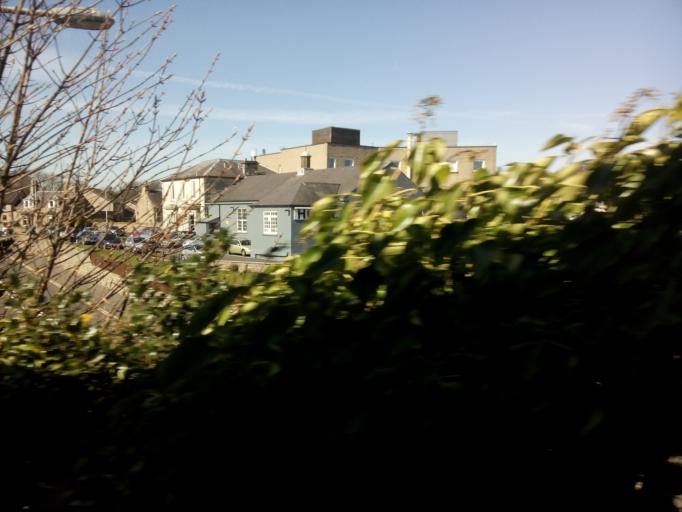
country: GB
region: Scotland
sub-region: Fife
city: Kirkcaldy
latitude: 56.1101
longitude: -3.1678
